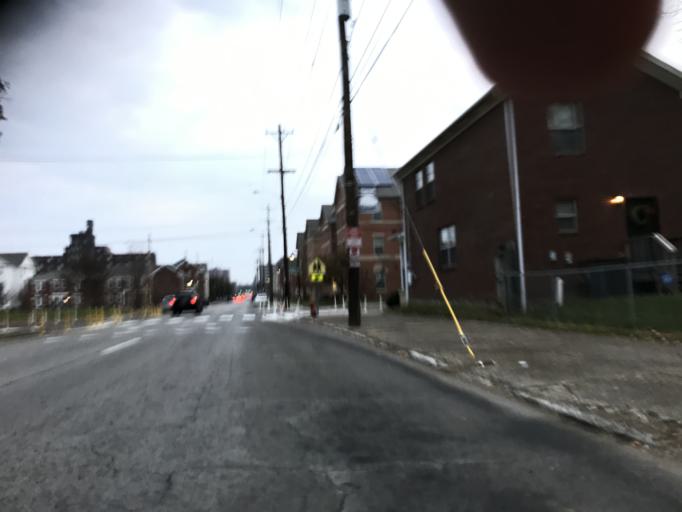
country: US
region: Kentucky
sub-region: Jefferson County
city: Louisville
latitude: 38.2416
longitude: -85.7462
